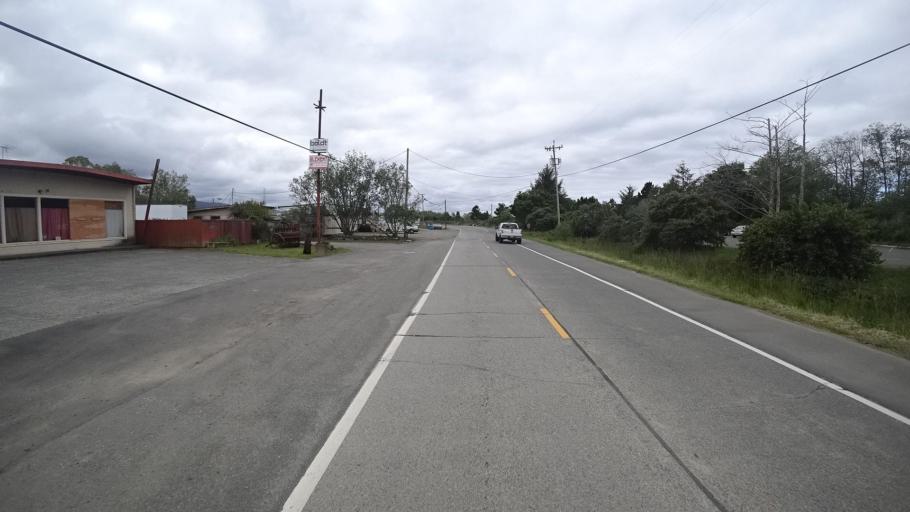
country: US
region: California
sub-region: Humboldt County
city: Arcata
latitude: 40.8590
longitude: -124.0895
